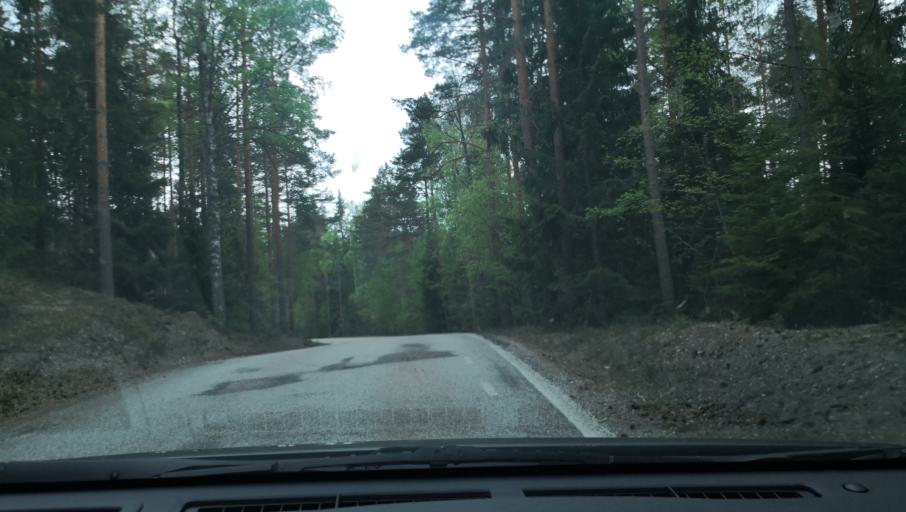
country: SE
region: Vaestmanland
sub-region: Skinnskattebergs Kommun
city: Skinnskatteberg
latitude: 59.8171
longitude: 15.5540
